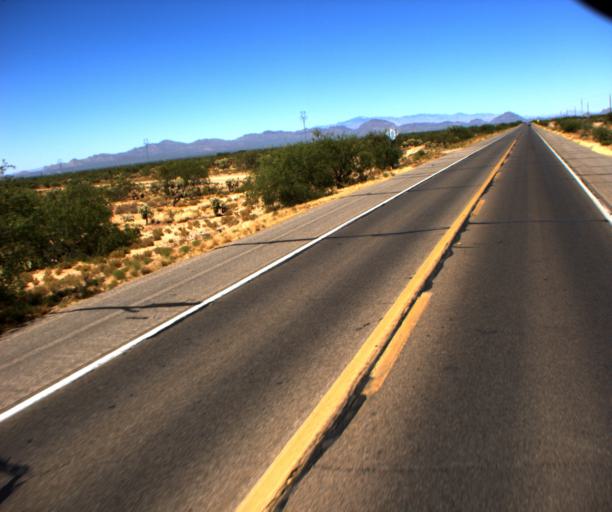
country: US
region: Arizona
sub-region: Pima County
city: Three Points
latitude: 32.0885
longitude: -111.2836
